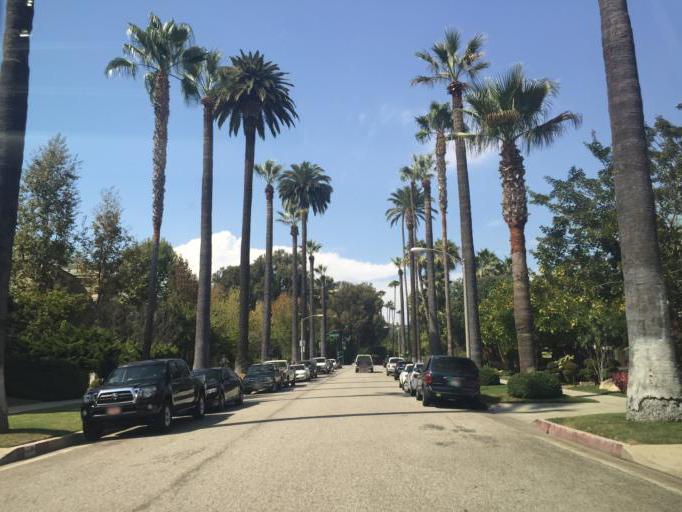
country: US
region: California
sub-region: Los Angeles County
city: Beverly Hills
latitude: 34.0861
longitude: -118.3981
